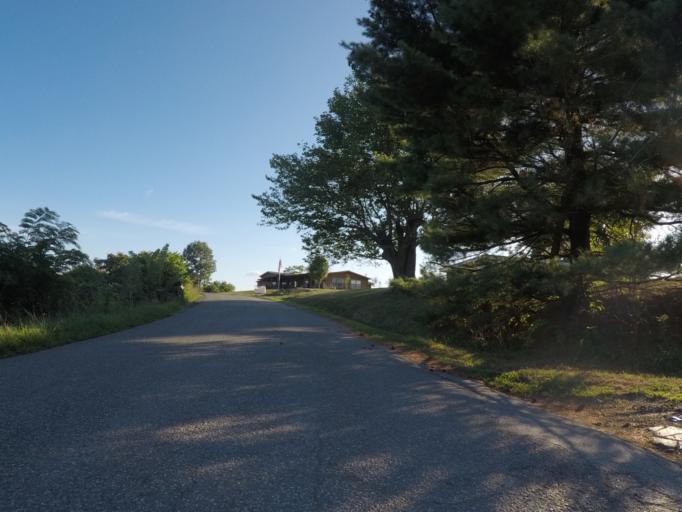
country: US
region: Ohio
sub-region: Lawrence County
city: Burlington
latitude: 38.5277
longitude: -82.5254
